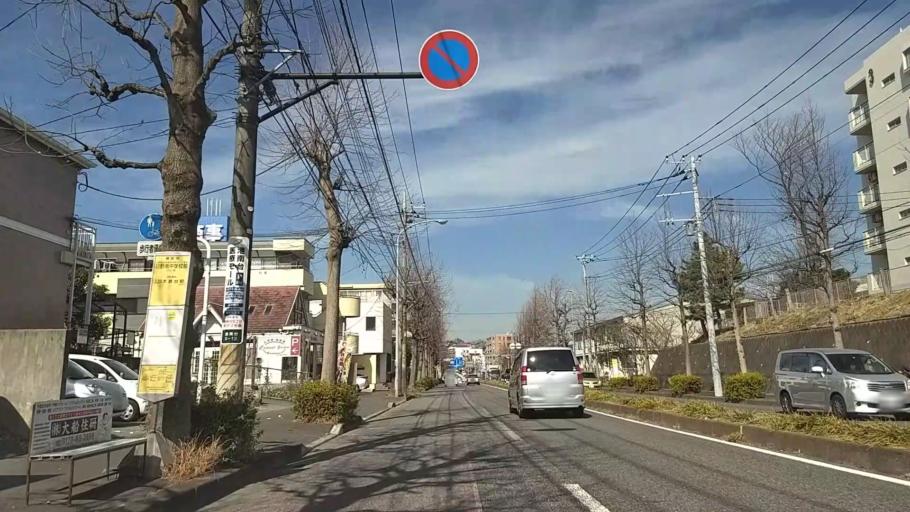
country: JP
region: Kanagawa
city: Kamakura
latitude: 35.3738
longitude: 139.5693
